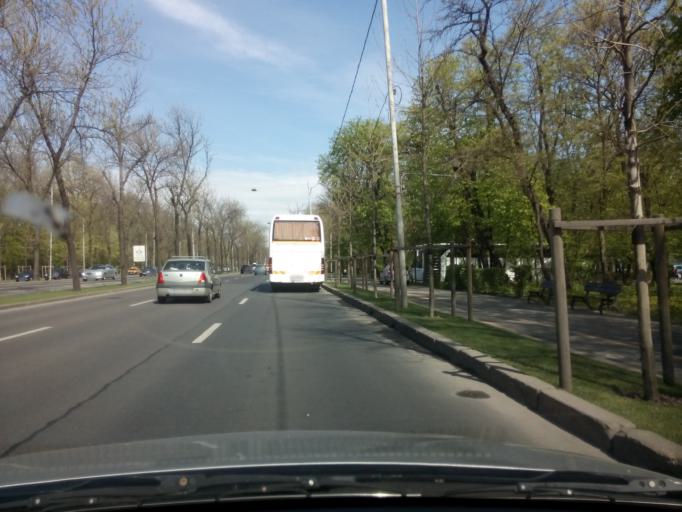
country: RO
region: Bucuresti
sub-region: Municipiul Bucuresti
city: Bucuresti
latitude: 44.4699
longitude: 26.0769
